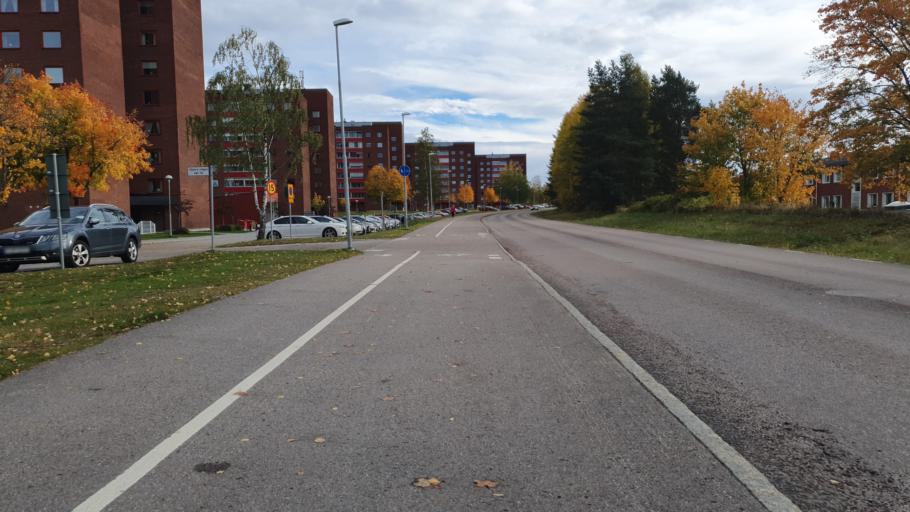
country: SE
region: Vaesternorrland
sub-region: Sundsvalls Kommun
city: Sundsvall
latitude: 62.4048
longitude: 17.2470
